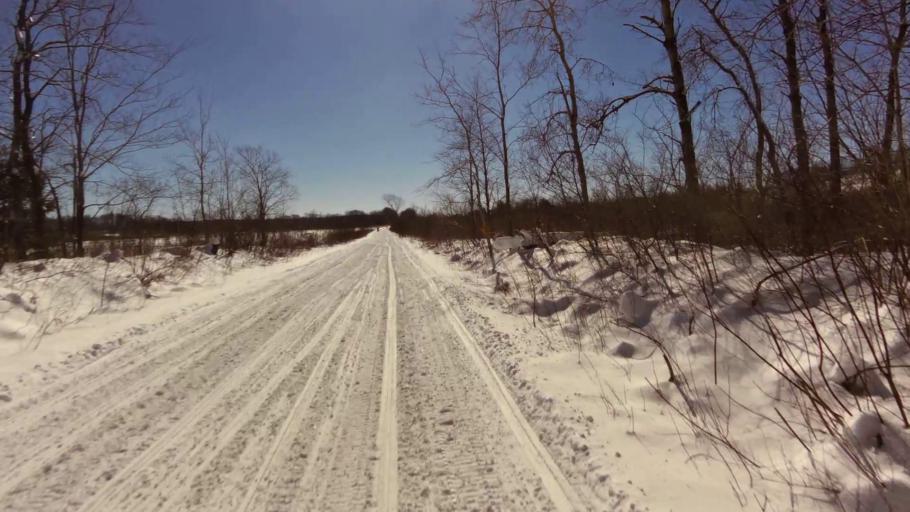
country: US
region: New York
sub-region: Chautauqua County
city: Mayville
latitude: 42.1789
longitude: -79.5813
